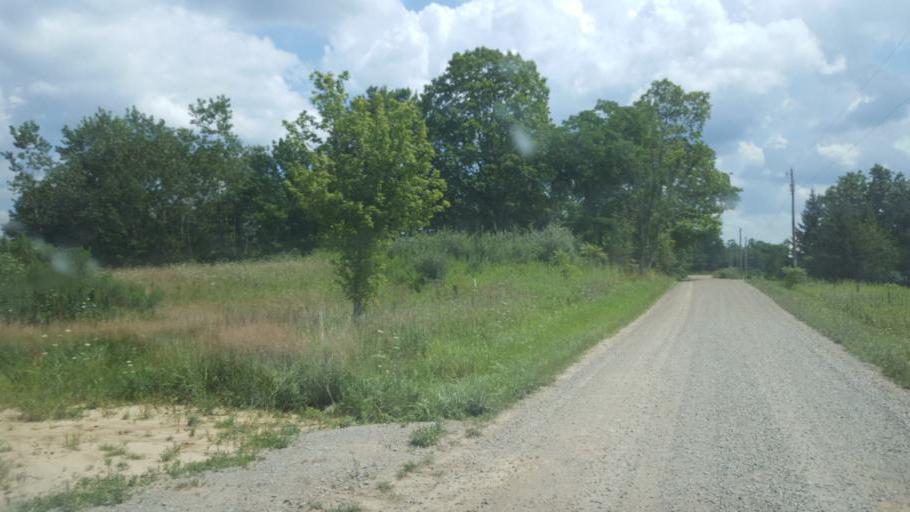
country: US
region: Ohio
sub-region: Knox County
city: Mount Vernon
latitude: 40.3624
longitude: -82.5822
